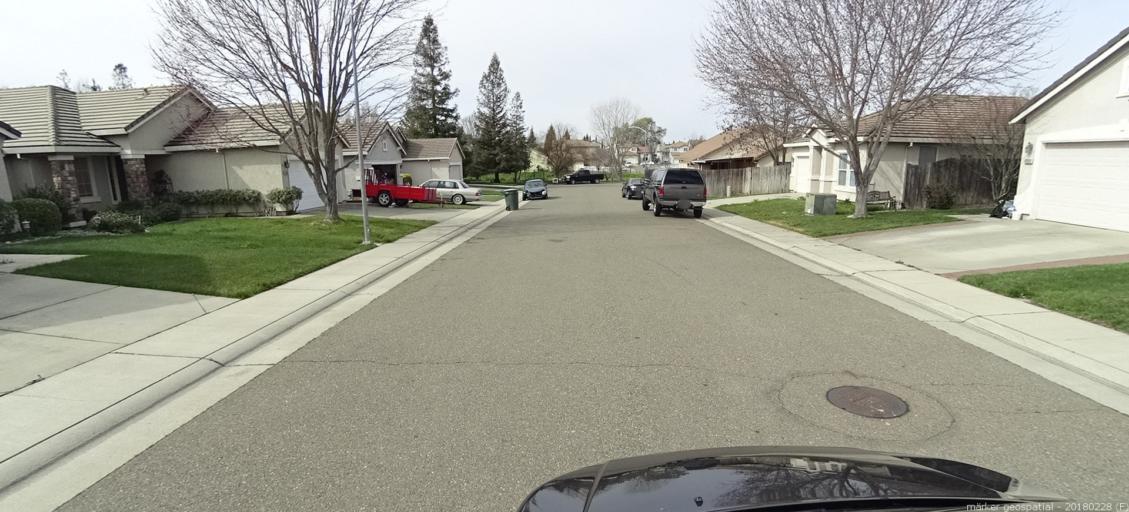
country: US
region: California
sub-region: Sacramento County
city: Antelope
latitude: 38.7186
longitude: -121.3300
